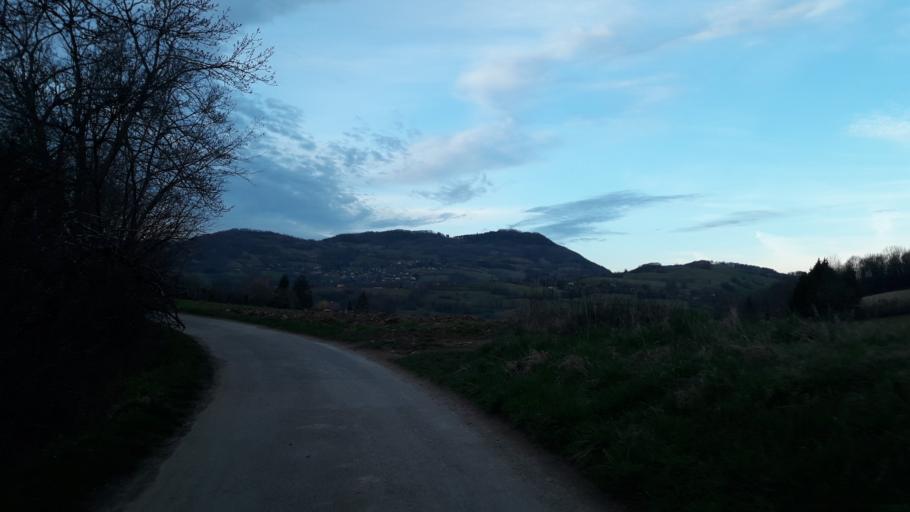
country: FR
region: Rhone-Alpes
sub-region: Departement de l'Isere
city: Brie-et-Angonnes
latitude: 45.1156
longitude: 5.7881
